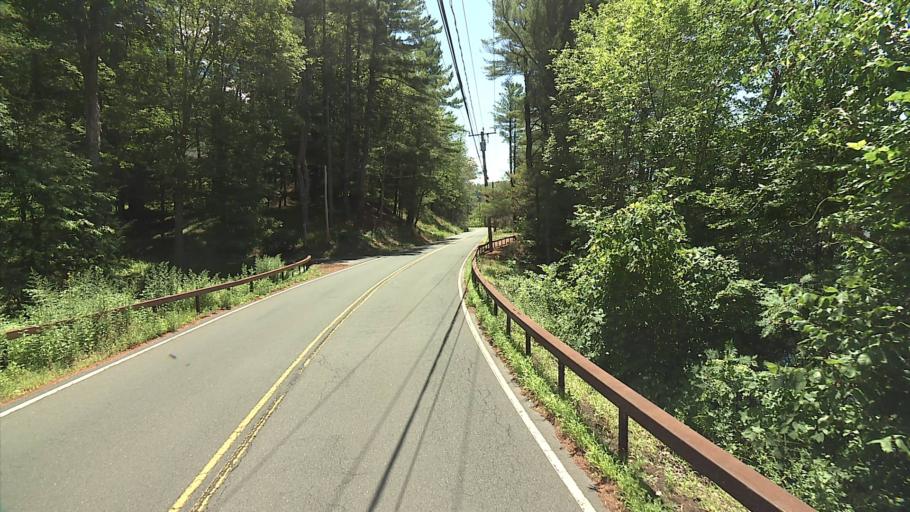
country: US
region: Connecticut
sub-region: Litchfield County
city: New Hartford Center
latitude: 41.8942
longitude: -72.9557
